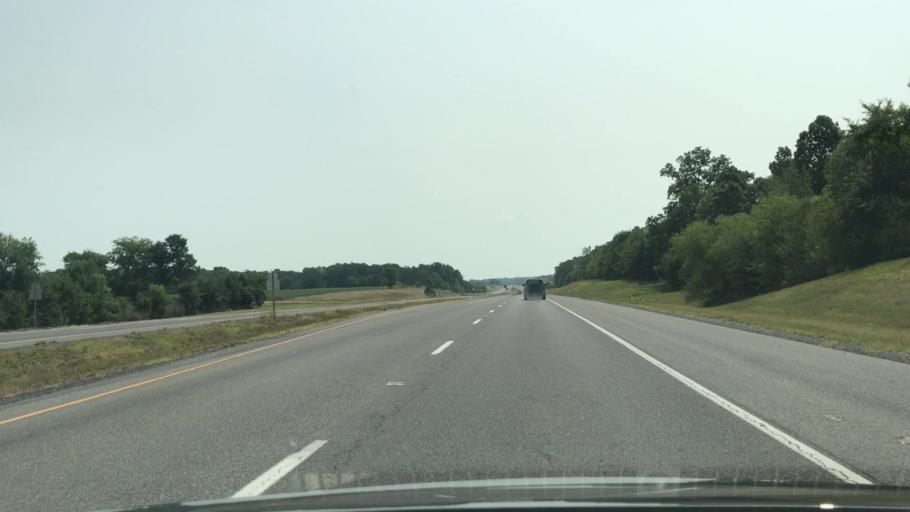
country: US
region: Kentucky
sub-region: Calloway County
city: Murray
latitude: 36.6508
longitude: -88.2694
